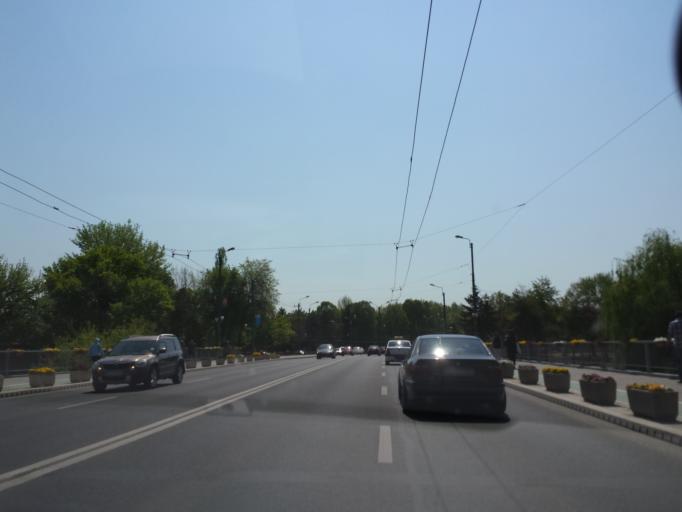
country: RO
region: Timis
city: Timisoara
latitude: 45.7505
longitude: 21.2345
